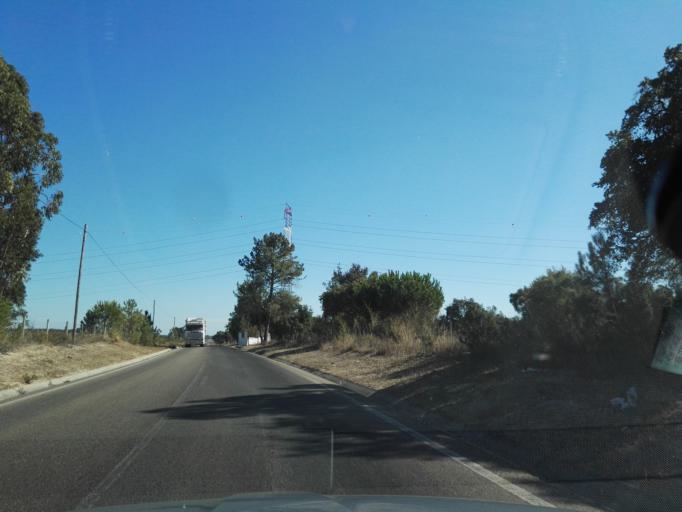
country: PT
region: Santarem
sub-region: Benavente
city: Benavente
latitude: 38.9218
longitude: -8.7741
